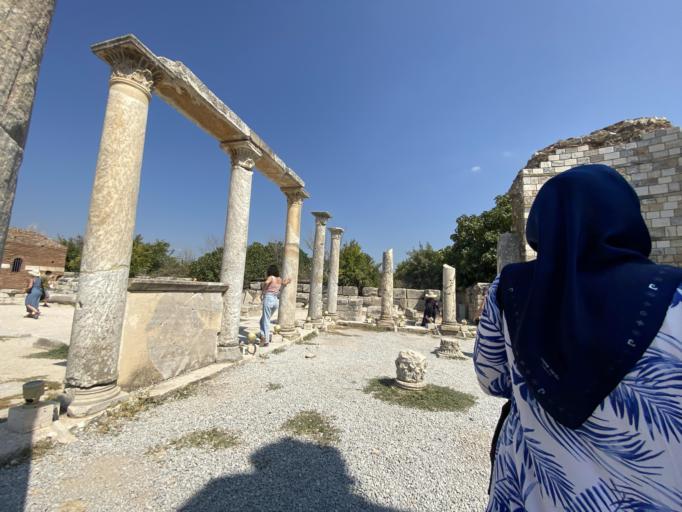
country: TR
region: Izmir
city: Selcuk
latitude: 37.9448
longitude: 27.3398
